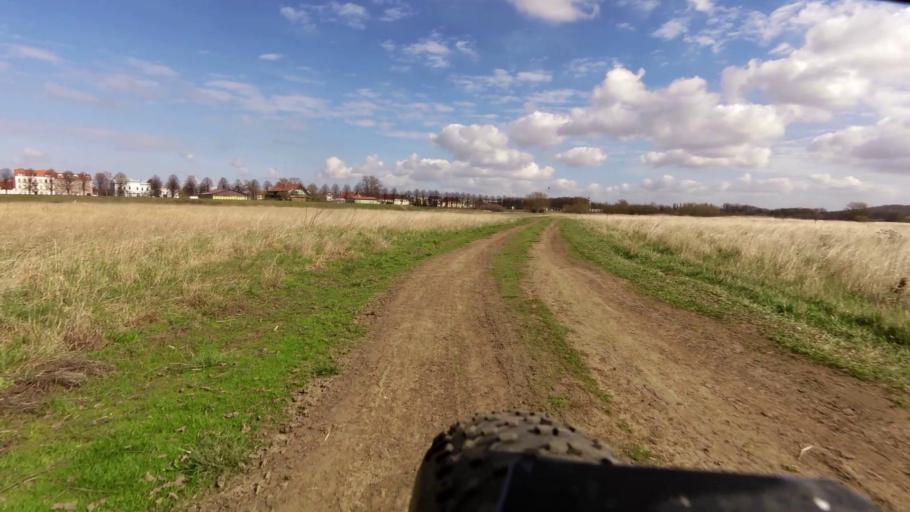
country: PL
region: Lubusz
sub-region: Powiat slubicki
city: Slubice
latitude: 52.3470
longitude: 14.5739
